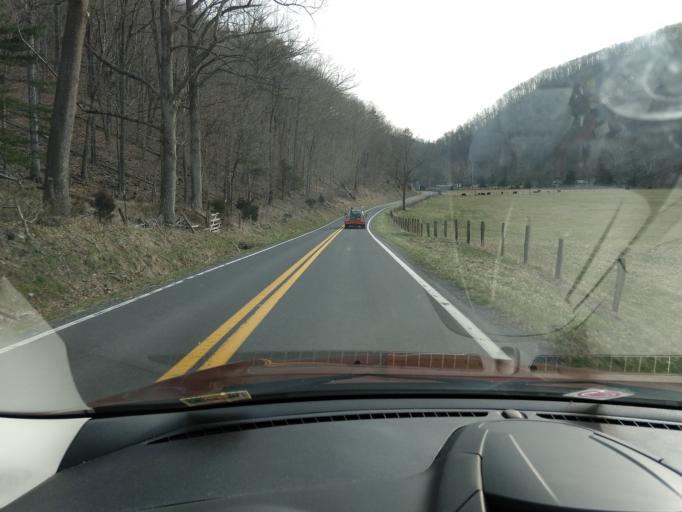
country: US
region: West Virginia
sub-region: Pendleton County
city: Franklin
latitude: 38.5988
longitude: -79.3841
